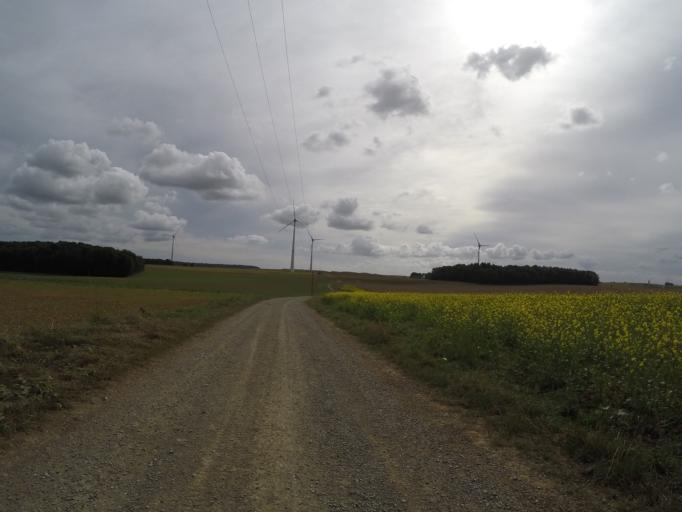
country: BE
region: Wallonia
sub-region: Province de Namur
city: Assesse
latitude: 50.3049
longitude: 4.9808
